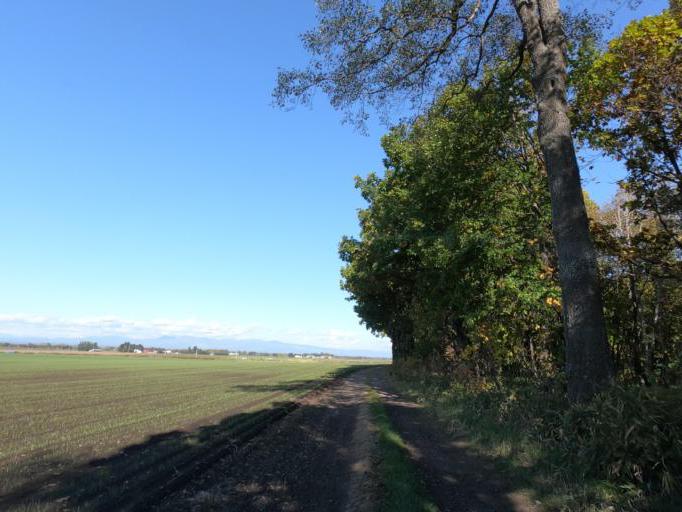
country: JP
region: Hokkaido
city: Otofuke
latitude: 43.0142
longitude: 143.2696
